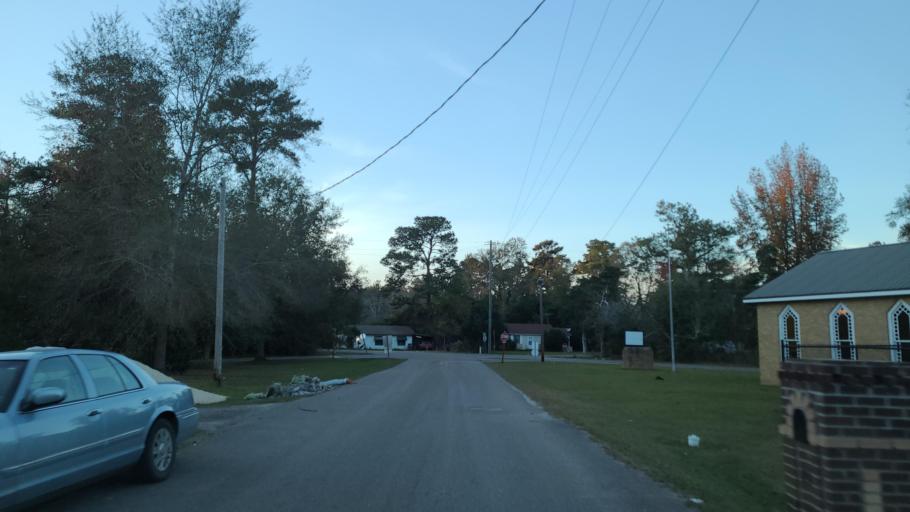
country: US
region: Mississippi
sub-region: Stone County
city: Wiggins
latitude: 31.0576
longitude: -89.1863
